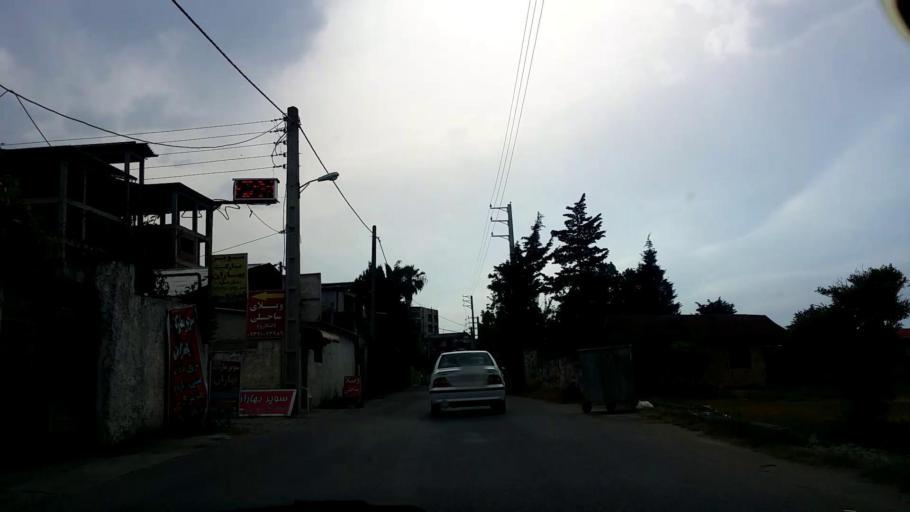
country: IR
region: Mazandaran
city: Chalus
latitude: 36.6863
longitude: 51.4079
